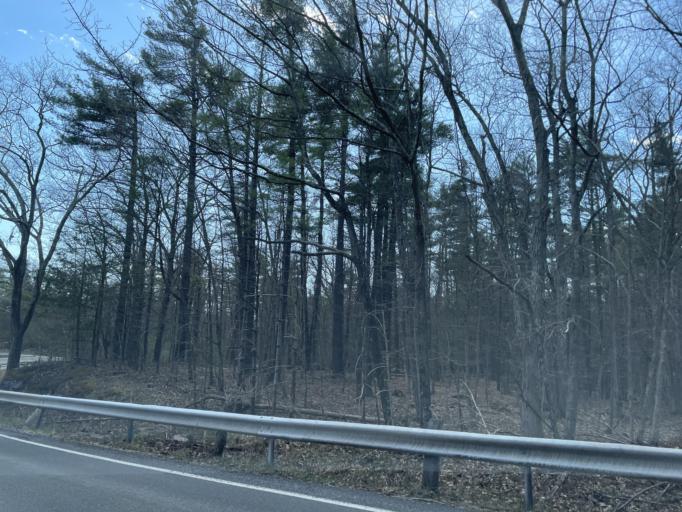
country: US
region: New York
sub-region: Ulster County
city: Zena
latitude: 42.0684
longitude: -74.0733
